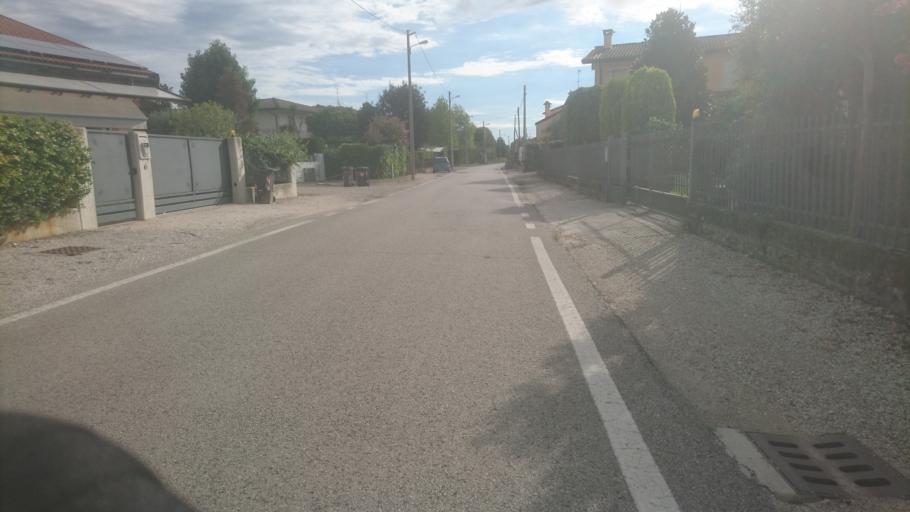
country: IT
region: Veneto
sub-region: Provincia di Padova
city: Villatora
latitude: 45.4003
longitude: 11.9653
